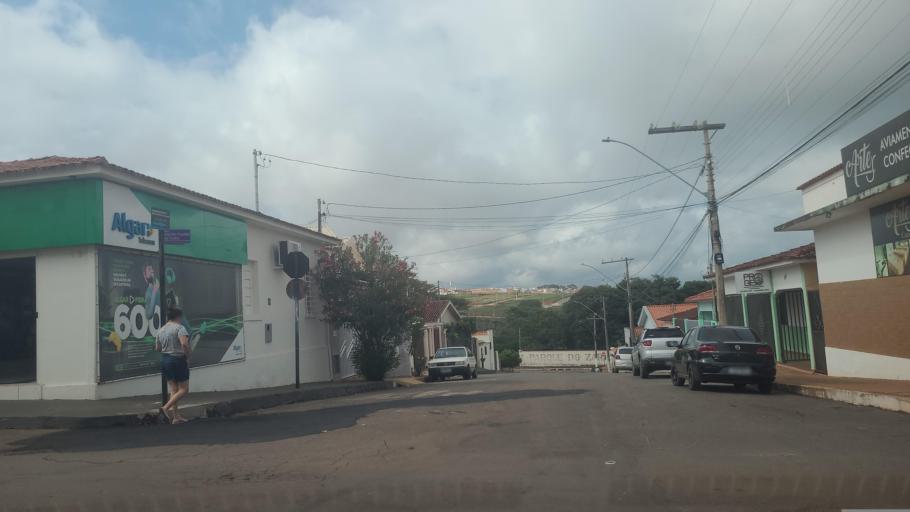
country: BR
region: Minas Gerais
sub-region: Carmo Do Paranaiba
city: Carmo do Paranaiba
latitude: -19.1942
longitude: -46.2453
